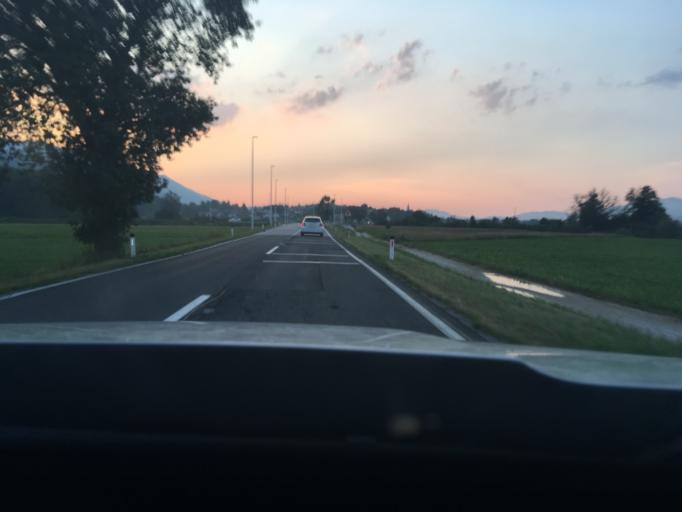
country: SI
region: Ribnica
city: Ribnica
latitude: 45.6970
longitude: 14.7647
